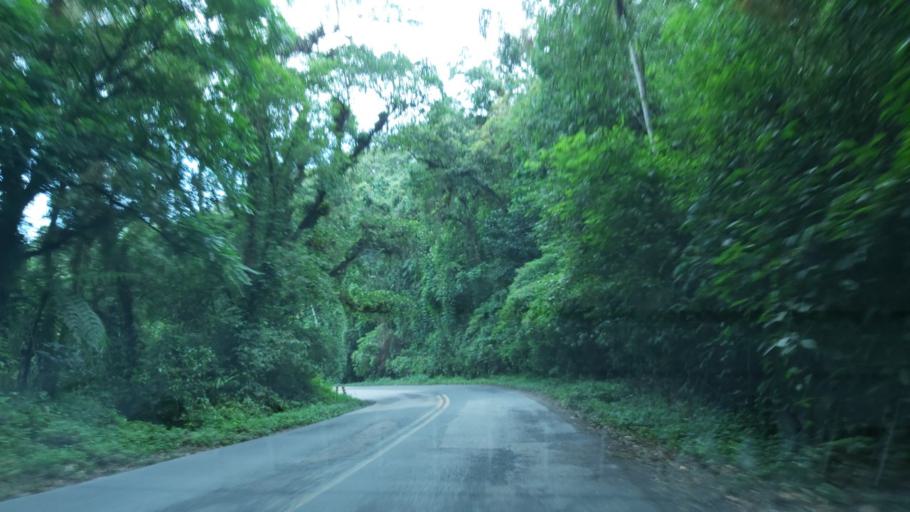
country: BR
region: Sao Paulo
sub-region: Juquia
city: Juquia
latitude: -24.0744
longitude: -47.6038
